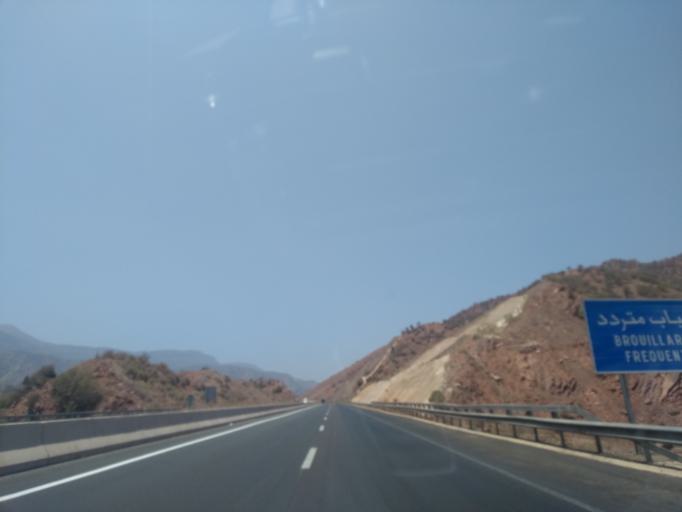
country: MA
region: Souss-Massa-Draa
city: Oulad Teima
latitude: 30.5436
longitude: -9.3261
